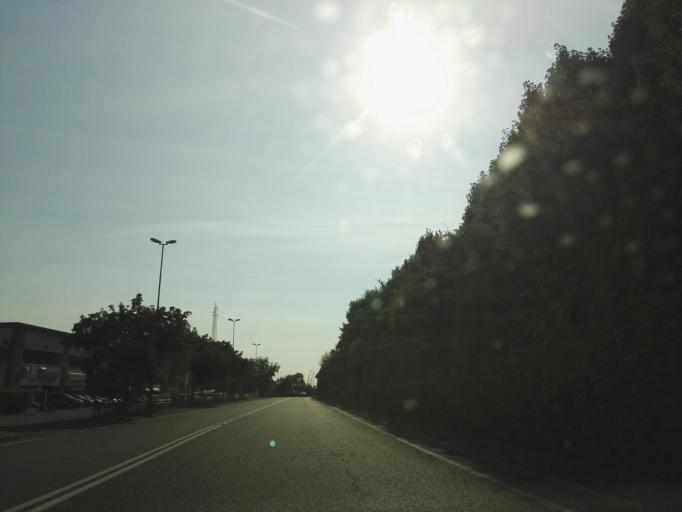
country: IT
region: Lombardy
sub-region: Citta metropolitana di Milano
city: San Giuliano Milanese
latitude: 45.3838
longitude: 9.3066
